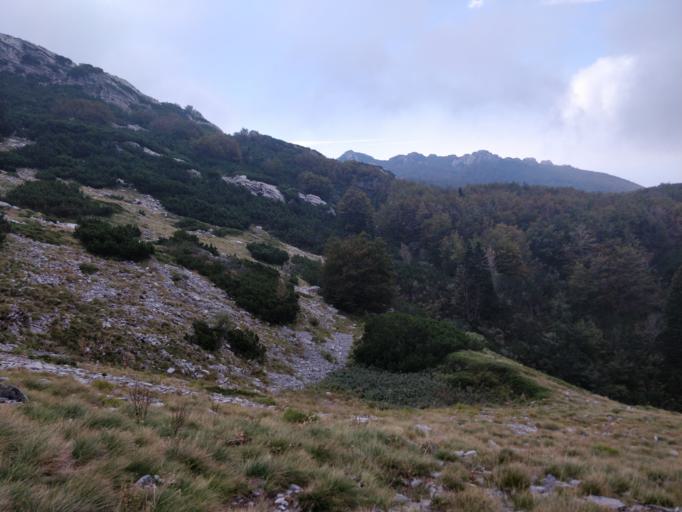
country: HR
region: Zadarska
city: Starigrad
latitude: 44.3768
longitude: 15.4813
